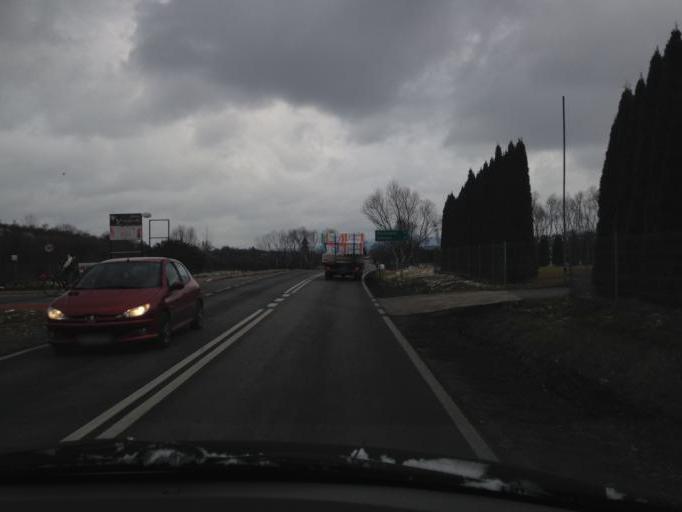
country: PL
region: Lesser Poland Voivodeship
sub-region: Powiat bochenski
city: Lapanow
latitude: 49.8617
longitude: 20.3288
